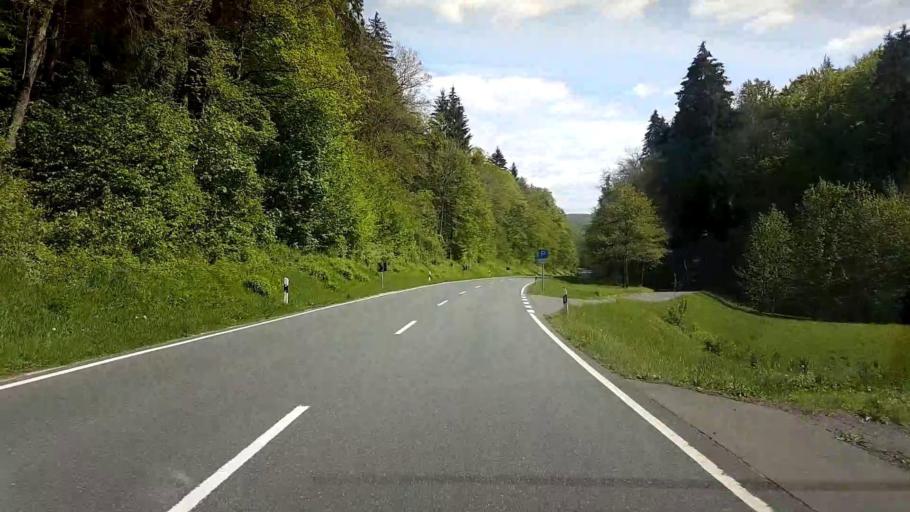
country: DE
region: Bavaria
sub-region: Upper Franconia
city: Ebermannstadt
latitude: 49.8055
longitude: 11.1637
